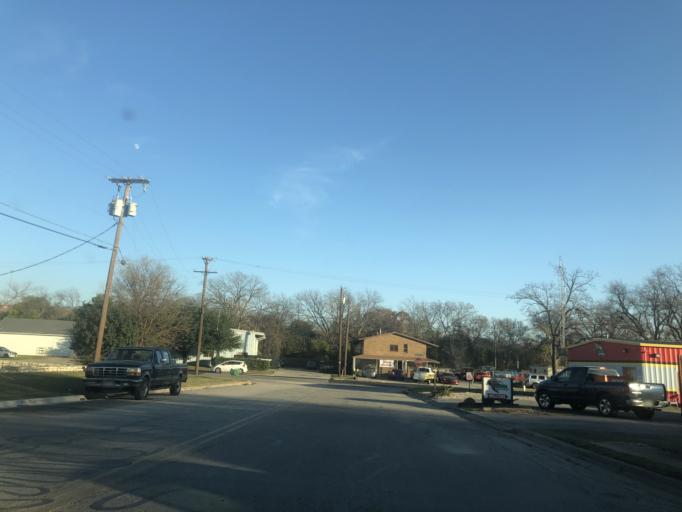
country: US
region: Texas
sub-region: Travis County
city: Wells Branch
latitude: 30.4287
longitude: -97.6763
